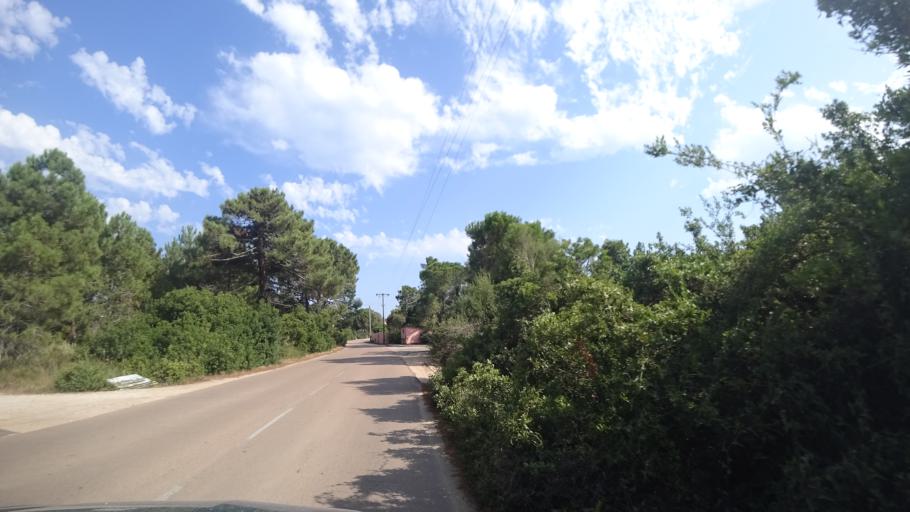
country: FR
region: Corsica
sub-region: Departement de la Corse-du-Sud
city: Porto-Vecchio
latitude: 41.6271
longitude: 9.3357
